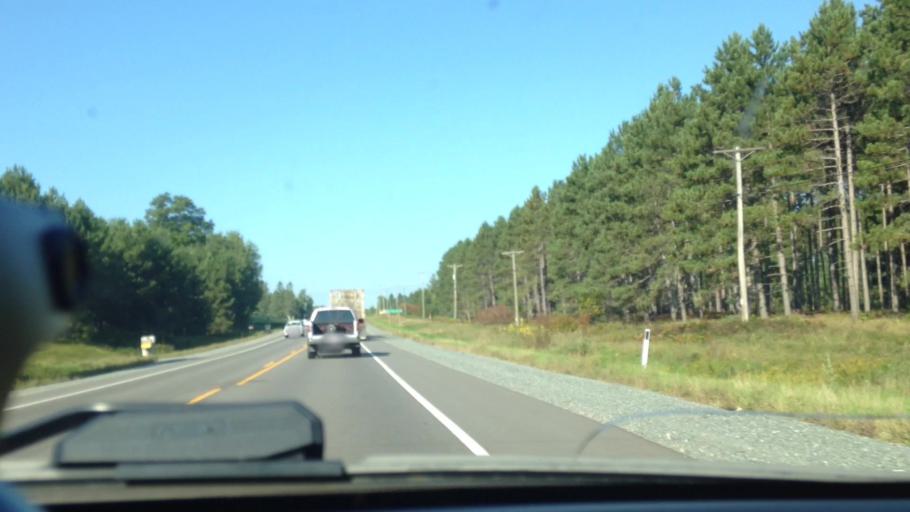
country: US
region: Michigan
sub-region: Dickinson County
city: Iron Mountain
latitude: 45.8760
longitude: -88.1034
